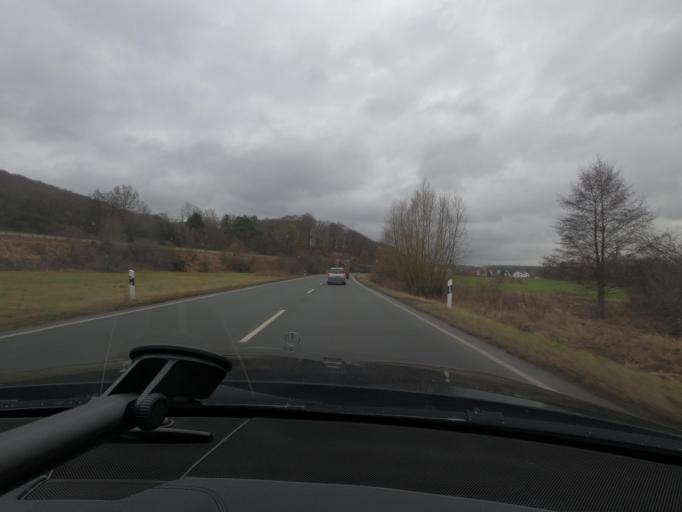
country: DE
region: Hesse
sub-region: Regierungsbezirk Kassel
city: Volkmarsen
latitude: 51.3912
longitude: 9.1411
